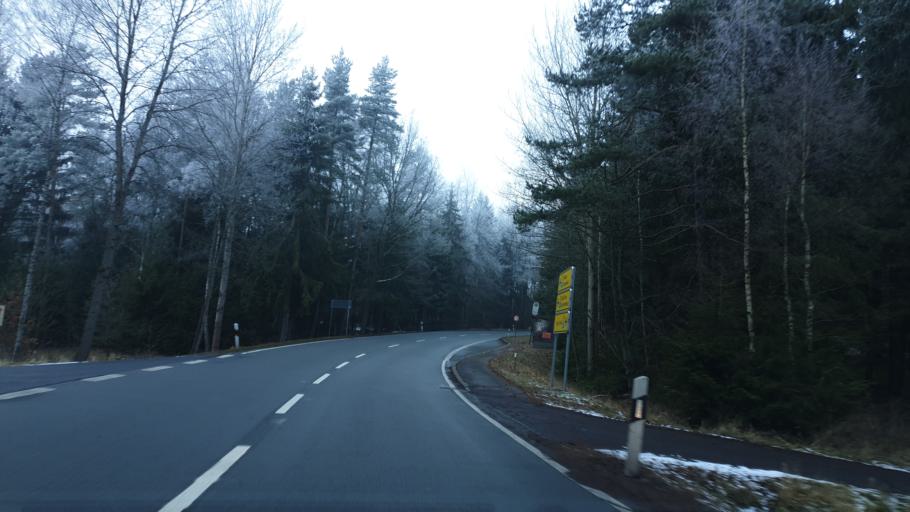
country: DE
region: Saxony
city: Bad Brambach
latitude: 50.2072
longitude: 12.3126
